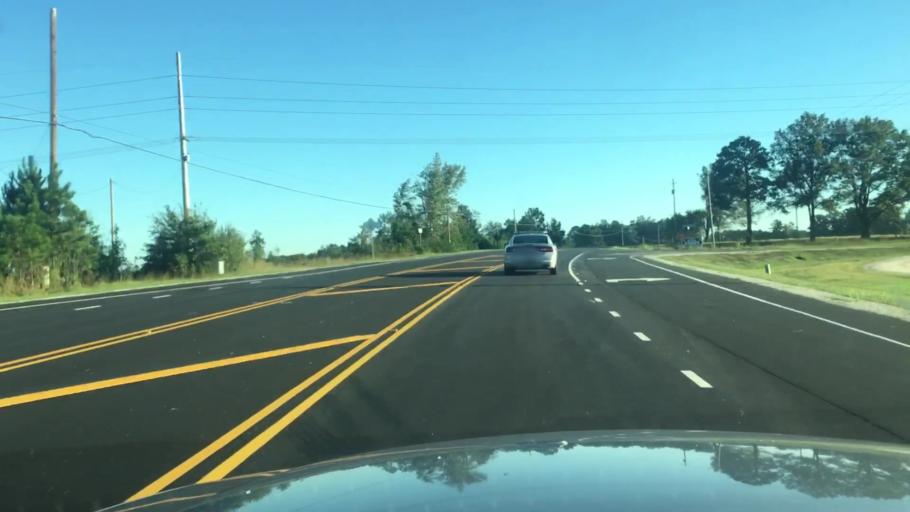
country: US
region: North Carolina
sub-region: Harnett County
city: Walkertown
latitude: 35.3264
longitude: -78.8672
